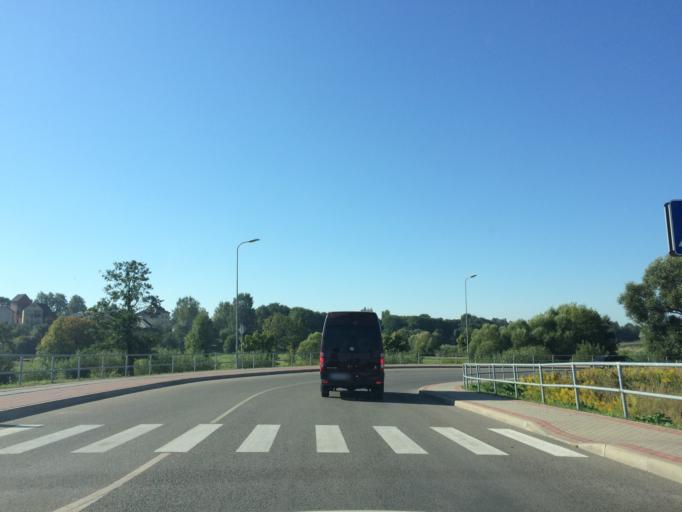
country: LV
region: Rezekne
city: Rezekne
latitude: 56.5140
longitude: 27.3544
